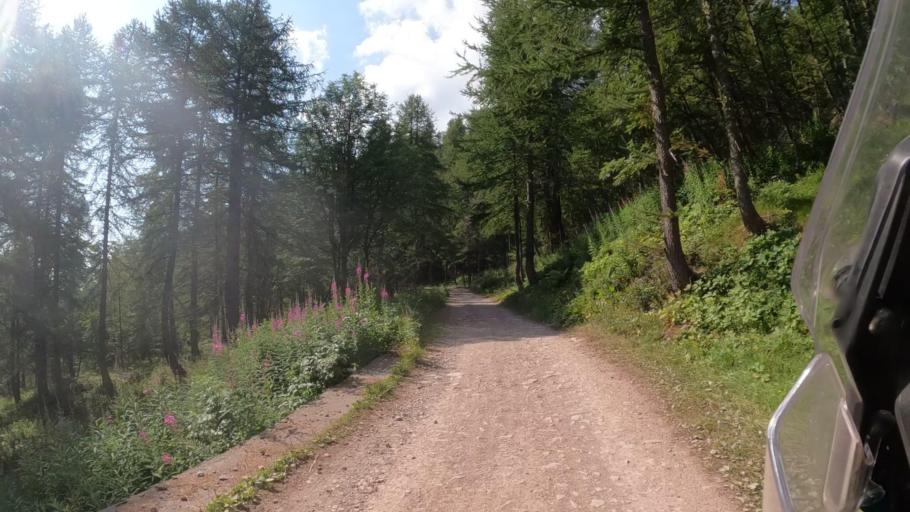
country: IT
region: Piedmont
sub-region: Provincia di Cuneo
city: Briga Alta
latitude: 44.1089
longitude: 7.7038
